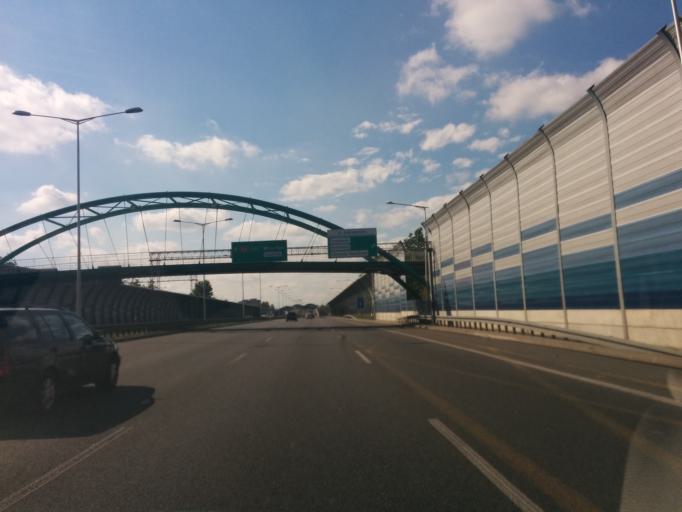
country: PL
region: Masovian Voivodeship
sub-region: Warszawa
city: Targowek
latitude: 52.3023
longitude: 21.0423
